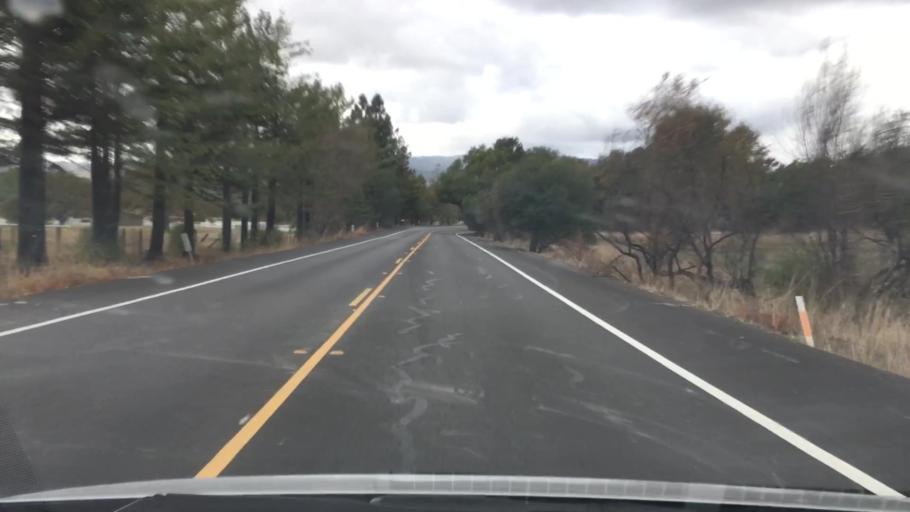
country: US
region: California
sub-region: Sonoma County
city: Sonoma
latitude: 38.2640
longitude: -122.4060
